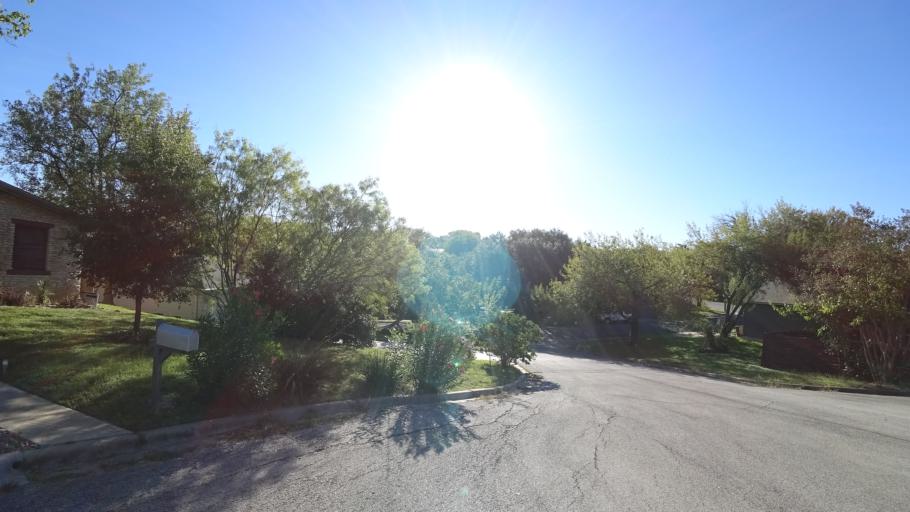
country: US
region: Texas
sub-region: Travis County
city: Austin
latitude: 30.3065
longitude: -97.6745
